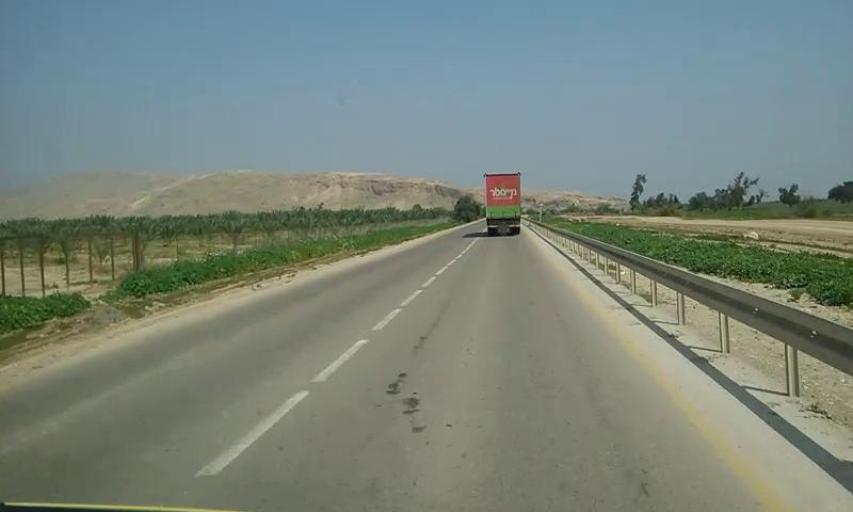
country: PS
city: Al Jiftlik
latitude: 32.1179
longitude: 35.5011
